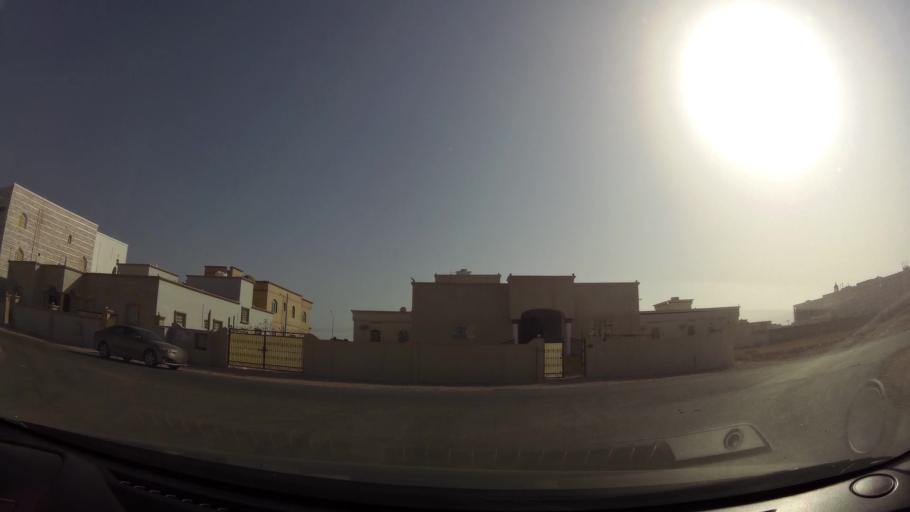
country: OM
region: Zufar
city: Salalah
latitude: 17.0073
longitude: 54.0249
